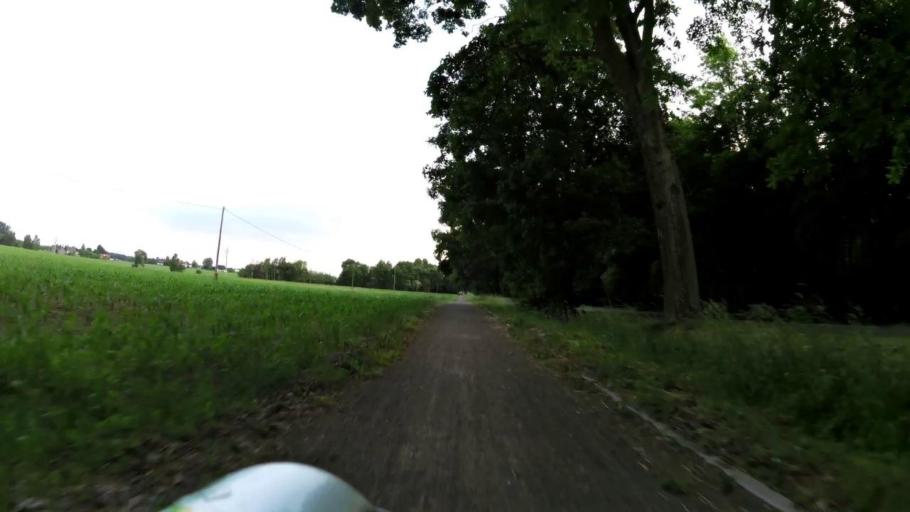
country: PL
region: Kujawsko-Pomorskie
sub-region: Powiat bydgoski
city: Dabrowa Chelminska
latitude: 53.1837
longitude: 18.3356
